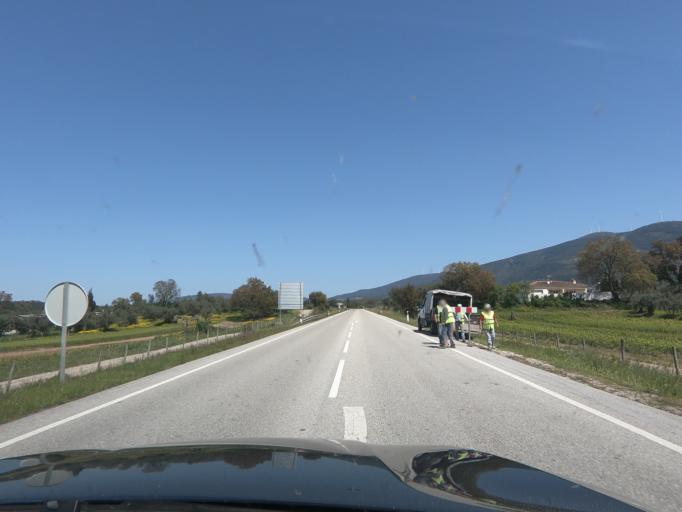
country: PT
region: Coimbra
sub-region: Lousa
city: Lousa
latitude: 40.1284
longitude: -8.2628
